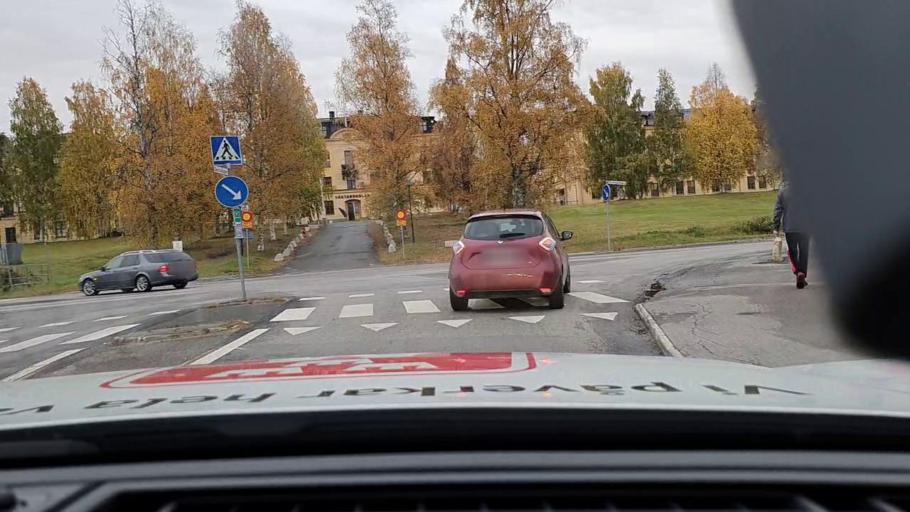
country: SE
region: Norrbotten
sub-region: Bodens Kommun
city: Boden
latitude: 65.8138
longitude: 21.6781
